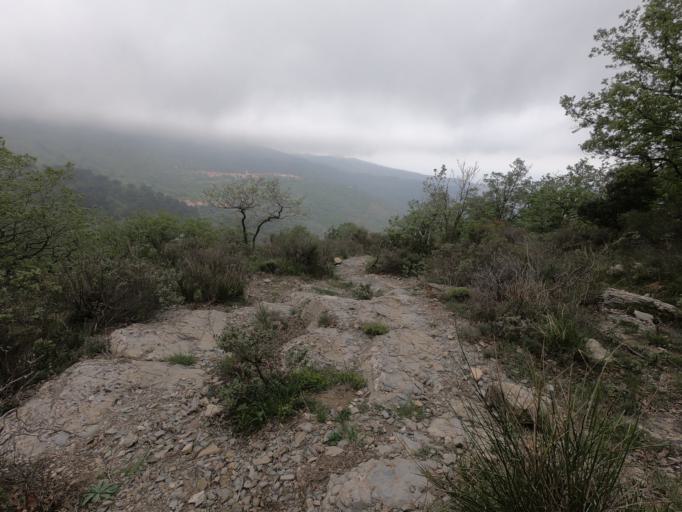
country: IT
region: Liguria
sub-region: Provincia di Imperia
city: Villa Faraldi
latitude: 43.9720
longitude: 8.0888
